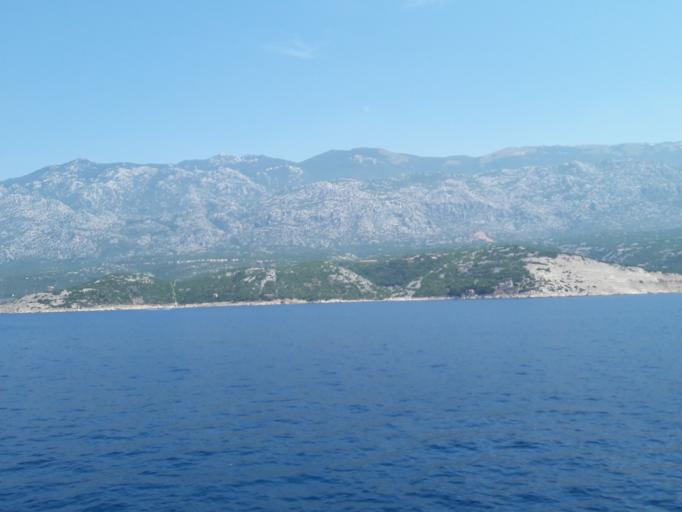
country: HR
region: Primorsko-Goranska
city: Banjol
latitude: 44.7072
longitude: 14.8755
